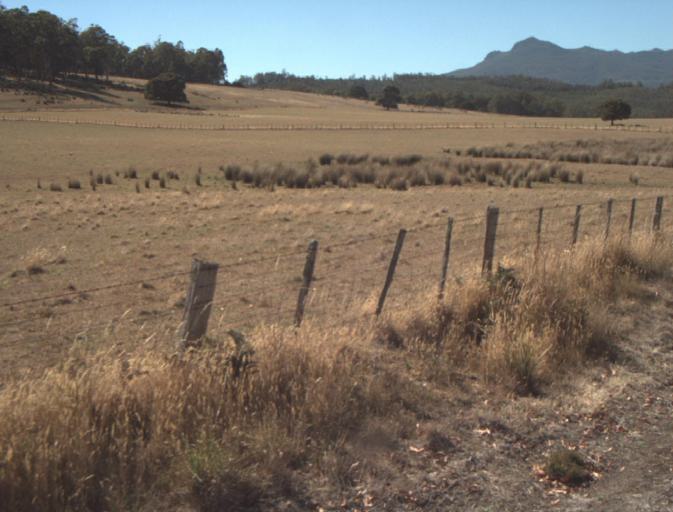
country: AU
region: Tasmania
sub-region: Launceston
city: Newstead
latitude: -41.3072
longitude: 147.3184
